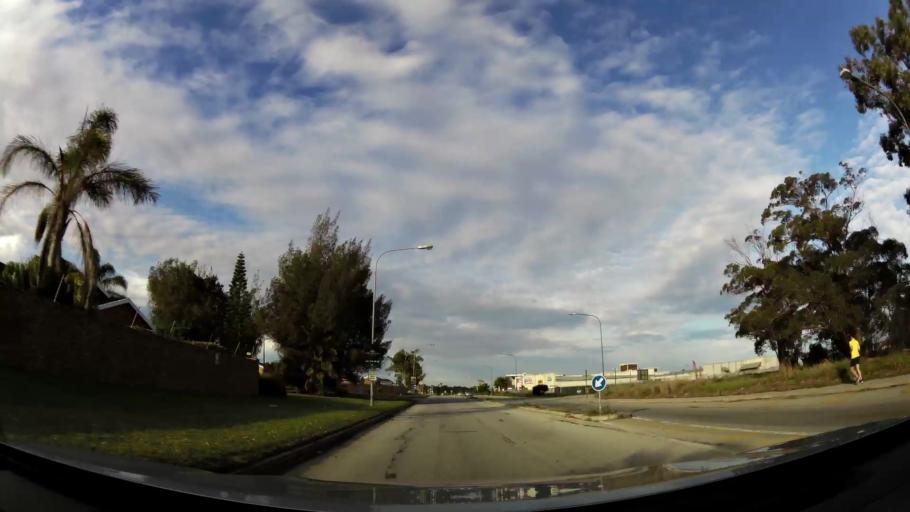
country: ZA
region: Eastern Cape
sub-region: Nelson Mandela Bay Metropolitan Municipality
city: Port Elizabeth
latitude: -33.9576
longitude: 25.5000
